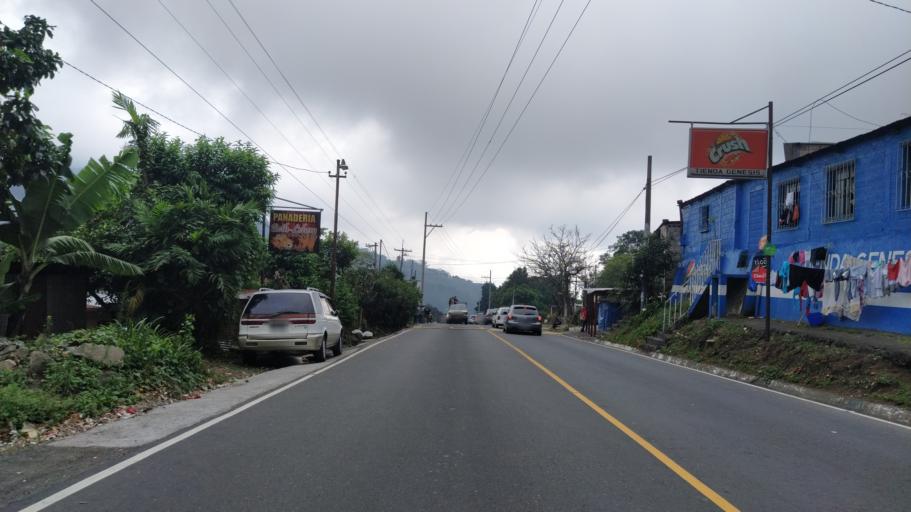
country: GT
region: Suchitepeque
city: Pueblo Nuevo
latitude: 14.7221
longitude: -91.5265
